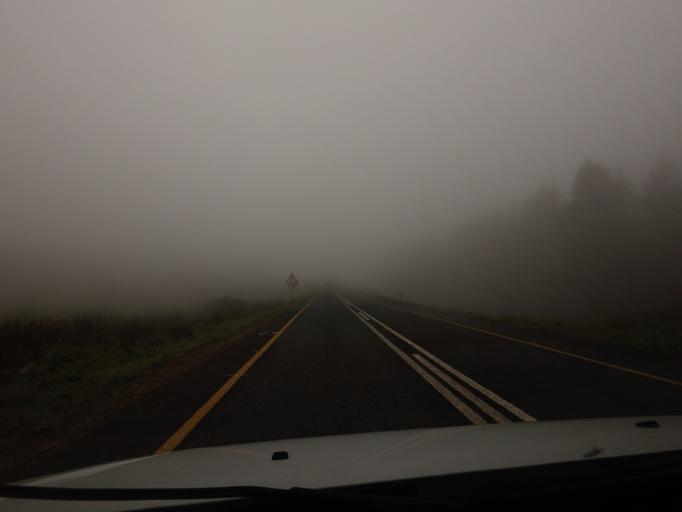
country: ZA
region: Mpumalanga
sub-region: Ehlanzeni District
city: Lydenburg
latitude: -25.1626
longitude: 30.6360
